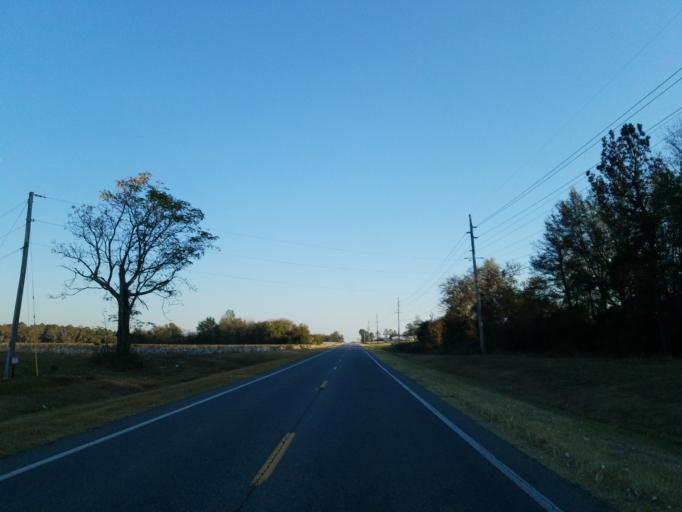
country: US
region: Georgia
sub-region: Crisp County
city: Cordele
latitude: 31.9470
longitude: -83.7429
